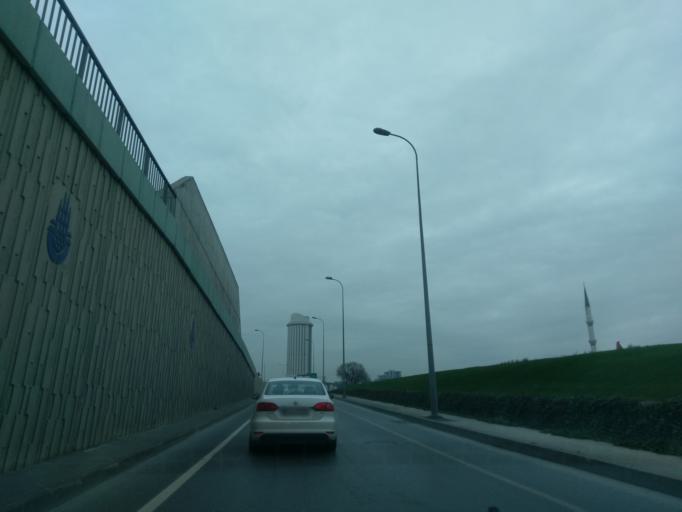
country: TR
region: Istanbul
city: Mahmutbey
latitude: 41.0608
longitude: 28.8158
